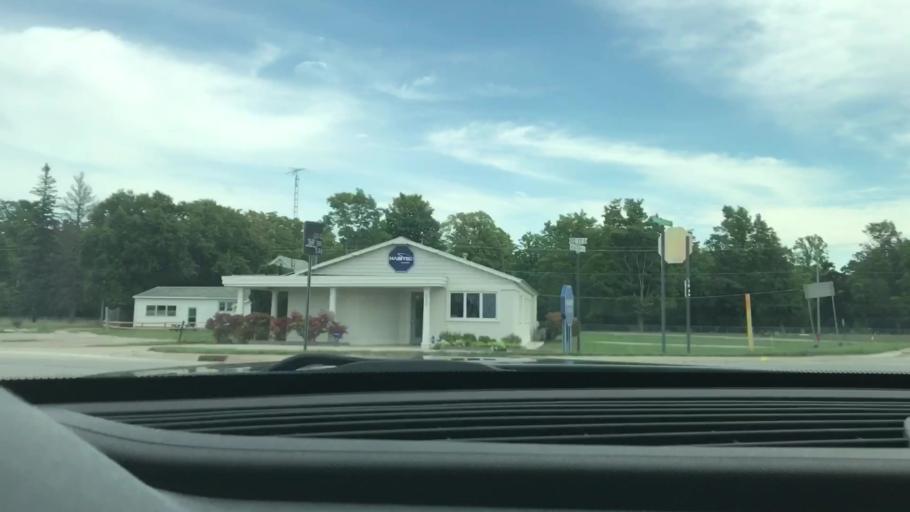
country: US
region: Michigan
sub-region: Charlevoix County
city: Charlevoix
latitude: 45.3024
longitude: -85.2646
